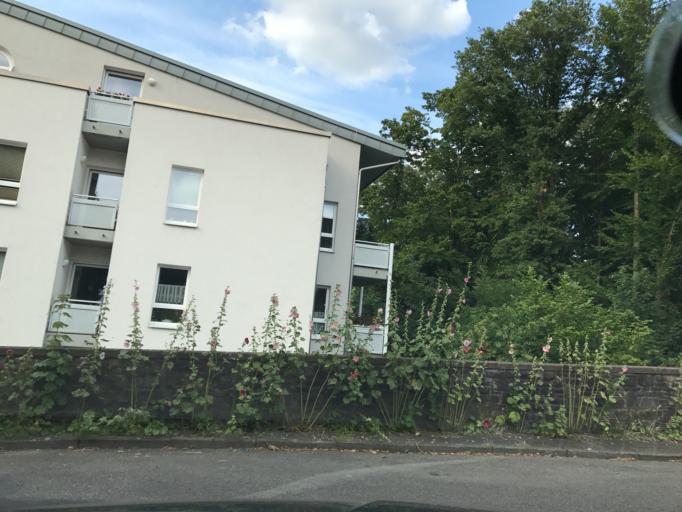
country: DE
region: North Rhine-Westphalia
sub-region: Regierungsbezirk Dusseldorf
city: Essen
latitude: 51.4333
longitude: 6.9807
